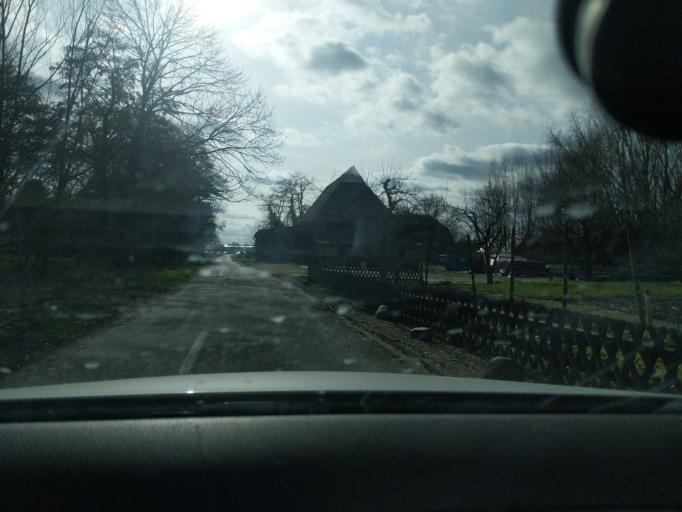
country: DE
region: Lower Saxony
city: Drochtersen
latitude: 53.7081
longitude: 9.4003
